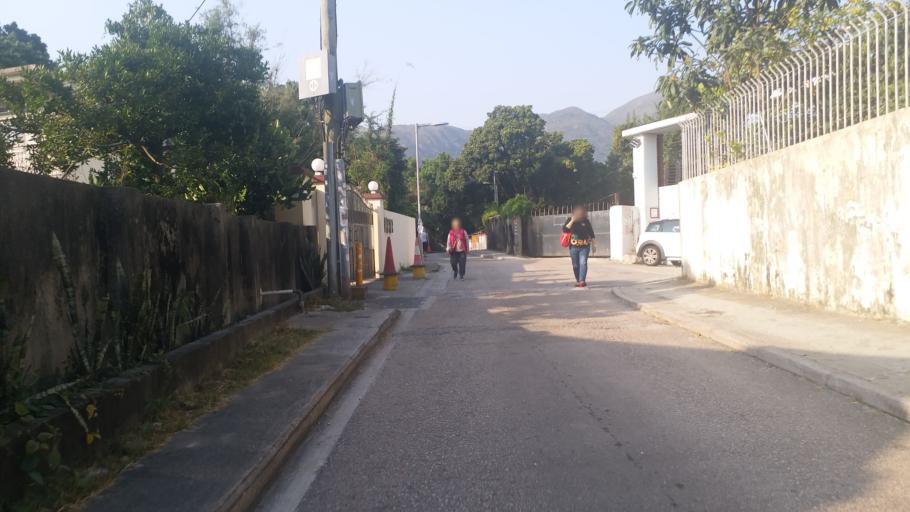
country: HK
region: Tuen Mun
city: Tuen Mun
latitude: 22.4160
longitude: 113.9742
